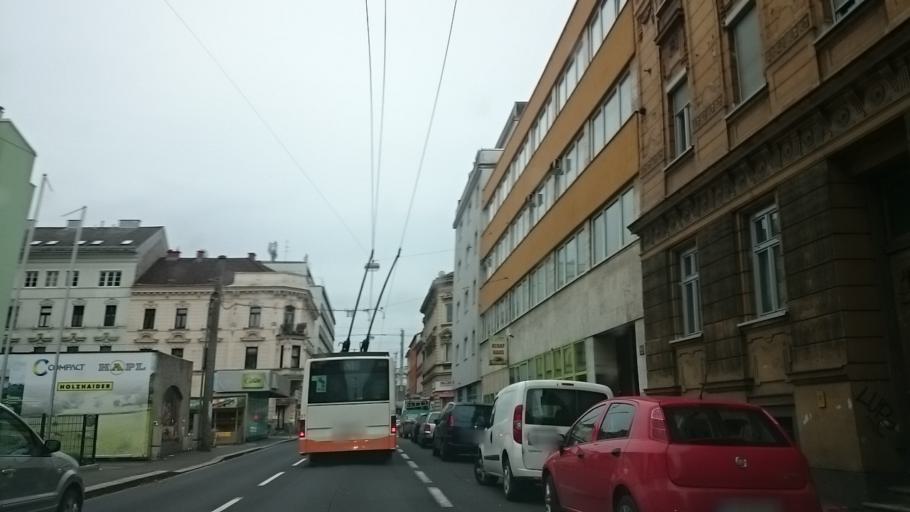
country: AT
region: Upper Austria
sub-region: Linz Stadt
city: Linz
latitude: 48.2969
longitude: 14.2958
